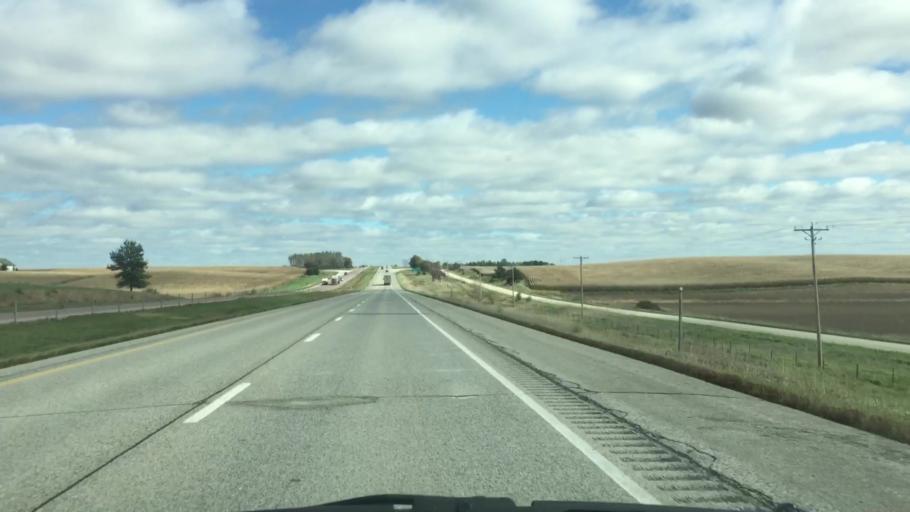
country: US
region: Iowa
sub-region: Iowa County
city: Marengo
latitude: 41.6960
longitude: -92.1759
